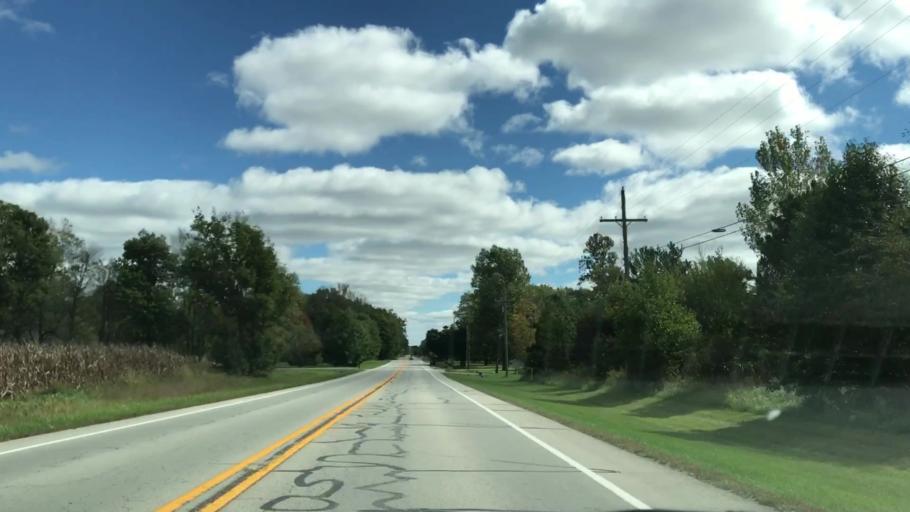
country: US
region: Indiana
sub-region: Hamilton County
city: Westfield
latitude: 40.0888
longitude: -86.1152
